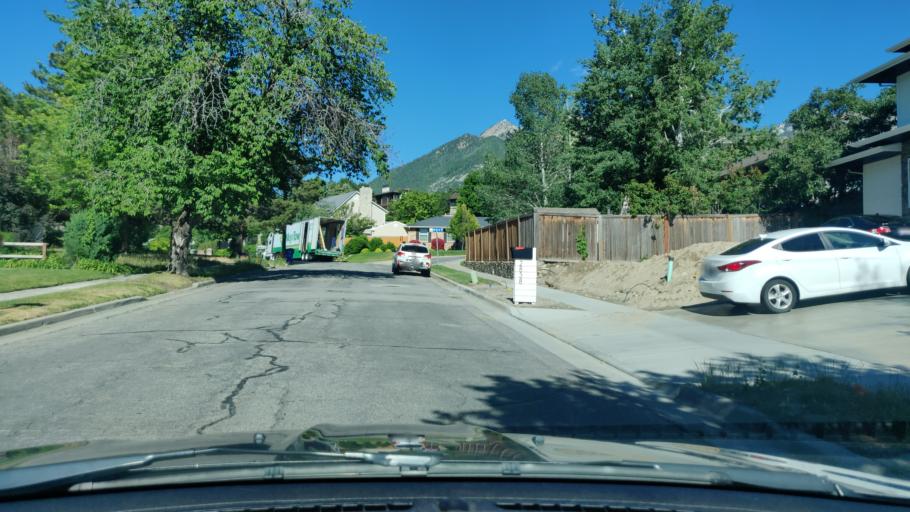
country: US
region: Utah
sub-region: Salt Lake County
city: Cottonwood Heights
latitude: 40.6141
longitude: -111.8124
